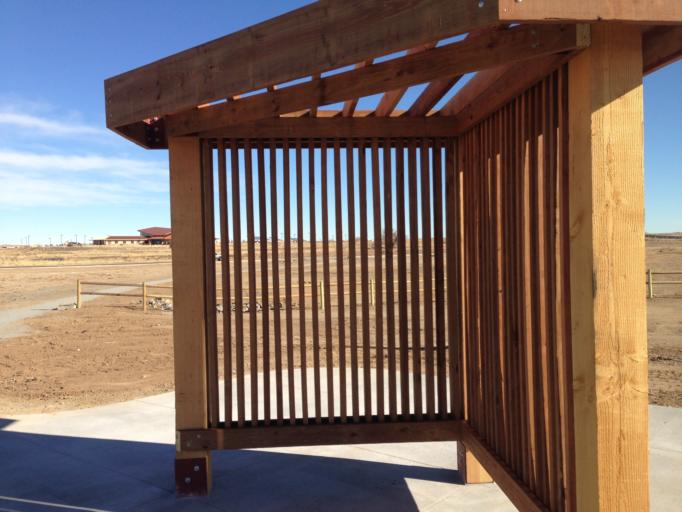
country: US
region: Colorado
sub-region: Adams County
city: Derby
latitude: 39.8133
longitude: -104.8843
